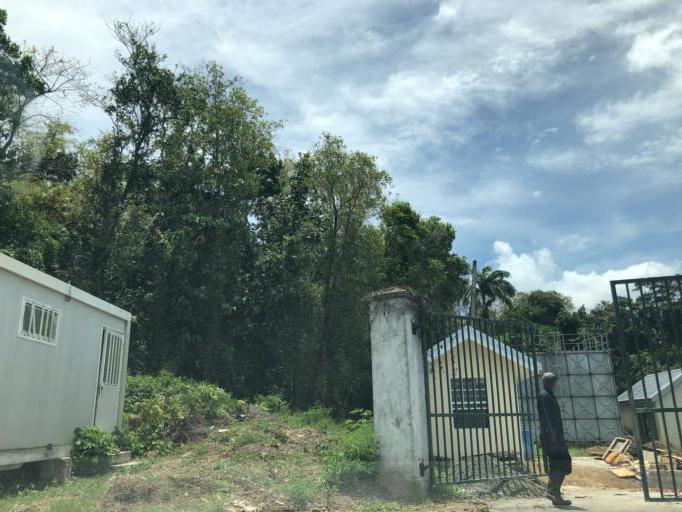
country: LC
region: Castries Quarter
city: Castries
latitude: 14.0018
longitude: -61.0086
